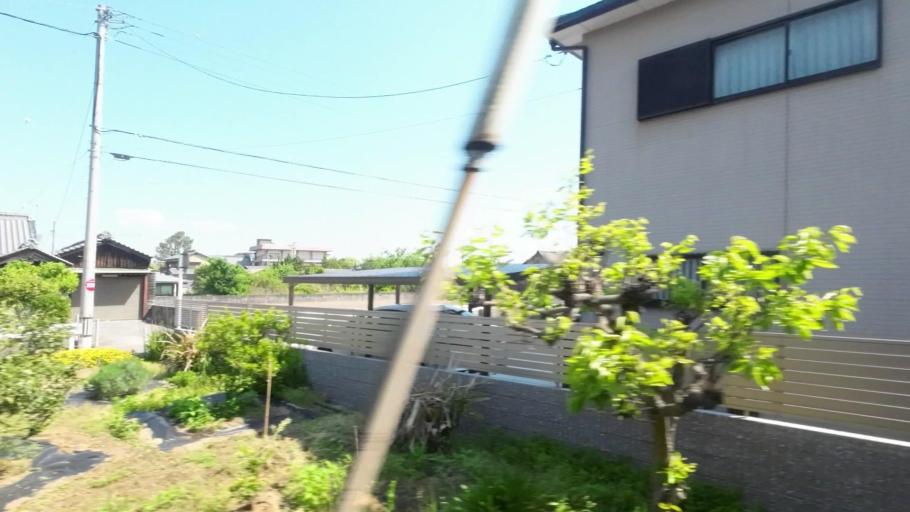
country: JP
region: Kagawa
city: Tadotsu
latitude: 34.2543
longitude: 133.7281
